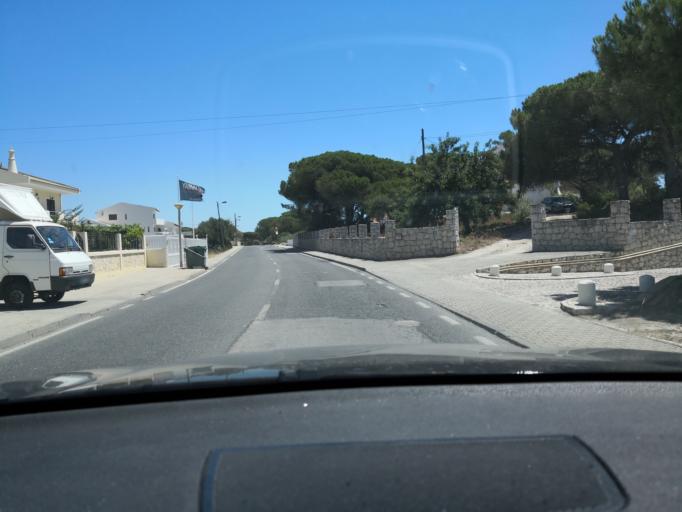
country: PT
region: Faro
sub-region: Albufeira
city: Ferreiras
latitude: 37.1083
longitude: -8.2081
